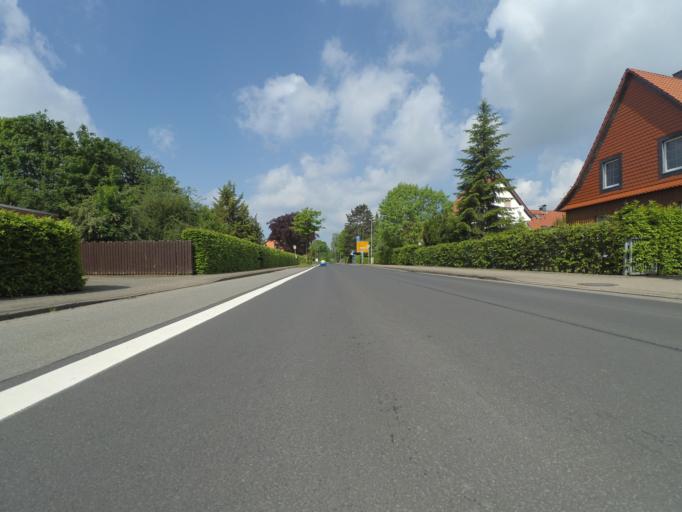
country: DE
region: Lower Saxony
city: Edemissen
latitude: 52.3880
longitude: 10.2561
